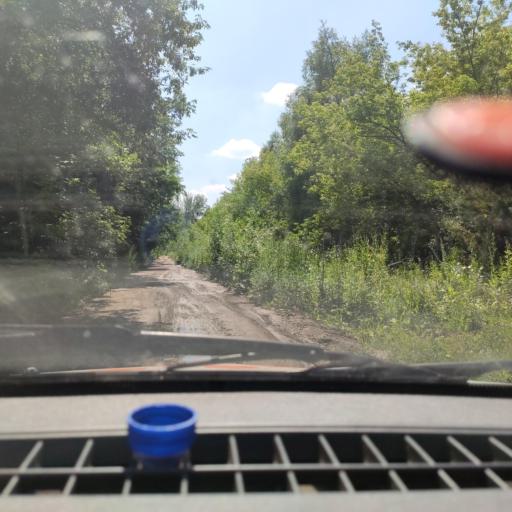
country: RU
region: Bashkortostan
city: Ufa
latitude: 54.6831
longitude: 55.9533
